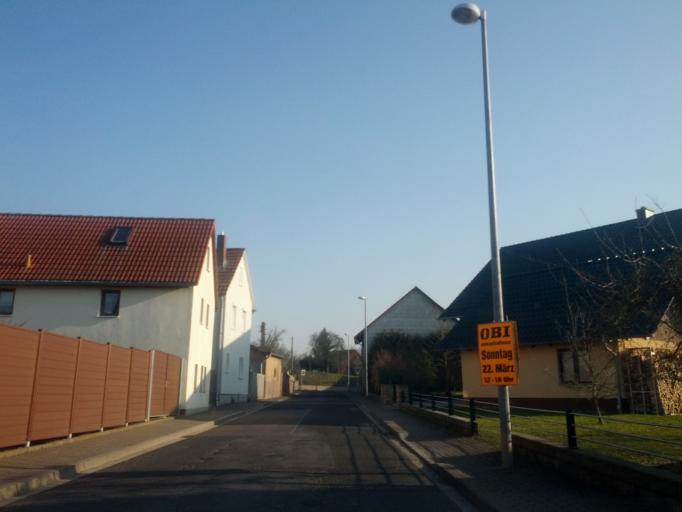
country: DE
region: Thuringia
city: Bischofroda
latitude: 51.0458
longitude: 10.3835
